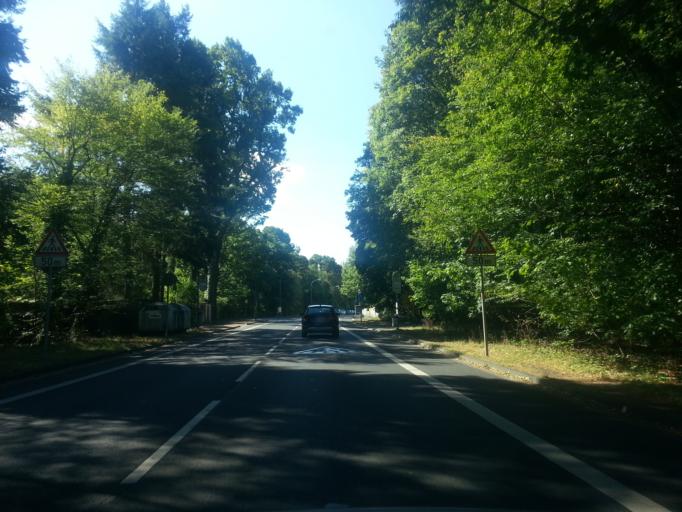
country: DE
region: Hesse
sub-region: Regierungsbezirk Darmstadt
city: Offenbach
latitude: 50.0785
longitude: 8.7659
